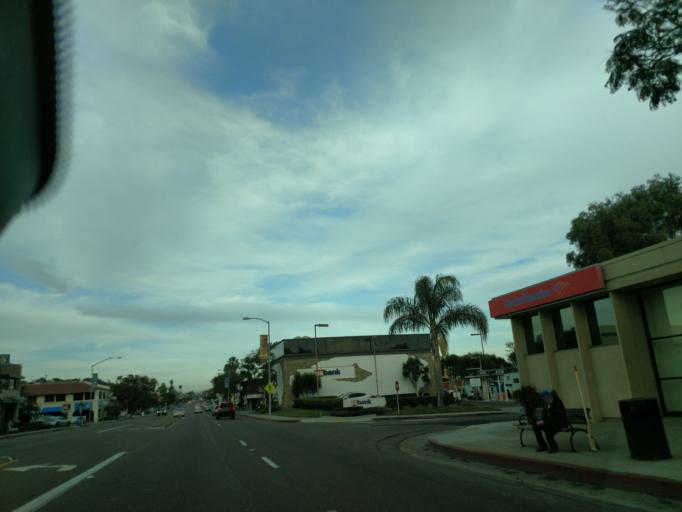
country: US
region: California
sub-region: San Diego County
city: Coronado
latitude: 32.7236
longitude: -117.2301
